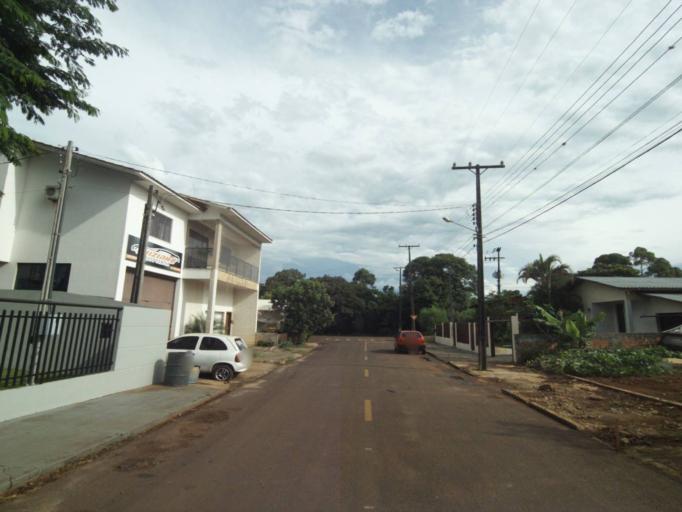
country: BR
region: Parana
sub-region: Guaraniacu
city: Guaraniacu
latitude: -25.1036
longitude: -52.8651
